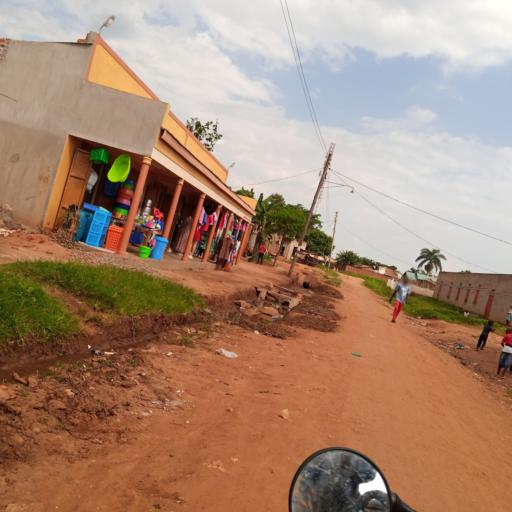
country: UG
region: Eastern Region
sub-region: Mbale District
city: Mbale
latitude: 1.0928
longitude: 34.1781
